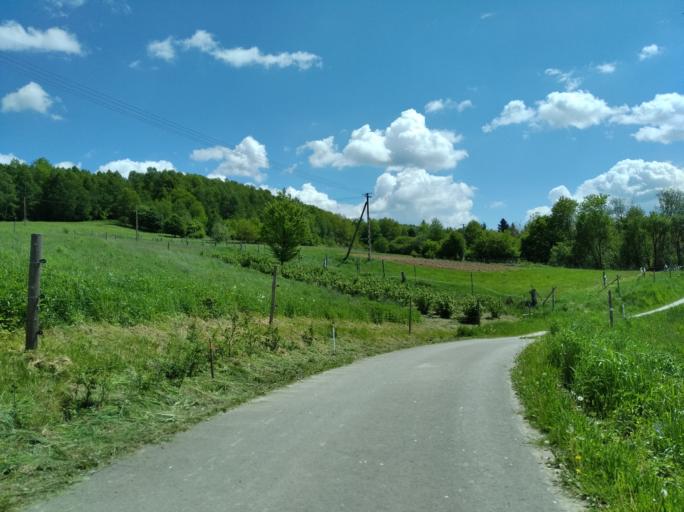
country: PL
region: Subcarpathian Voivodeship
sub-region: Powiat krosnienski
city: Leki
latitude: 49.8382
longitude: 21.6465
